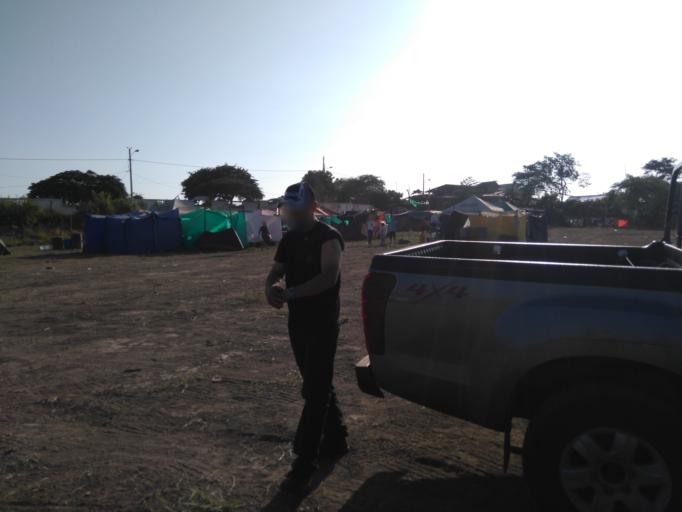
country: EC
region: Manabi
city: Bahia de Caraquez
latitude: -0.4618
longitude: -80.4516
